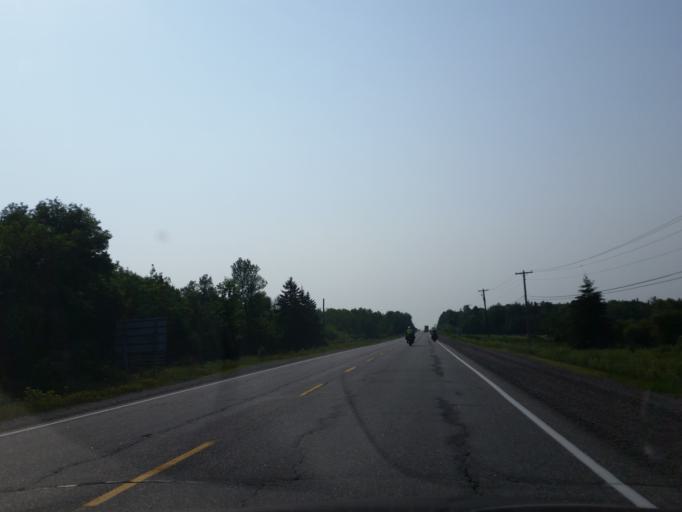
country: CA
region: Ontario
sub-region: Nipissing District
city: North Bay
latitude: 46.3866
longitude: -79.9926
